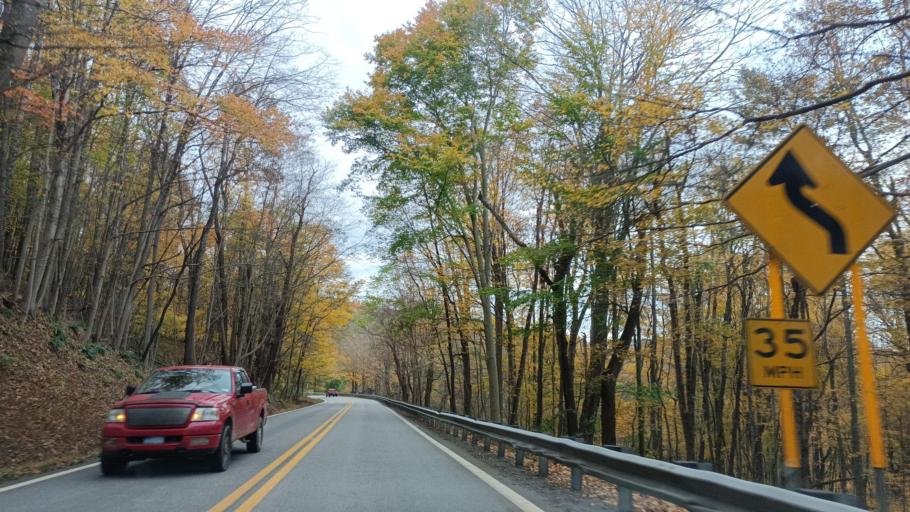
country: US
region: West Virginia
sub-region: Taylor County
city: Grafton
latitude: 39.3312
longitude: -79.9277
